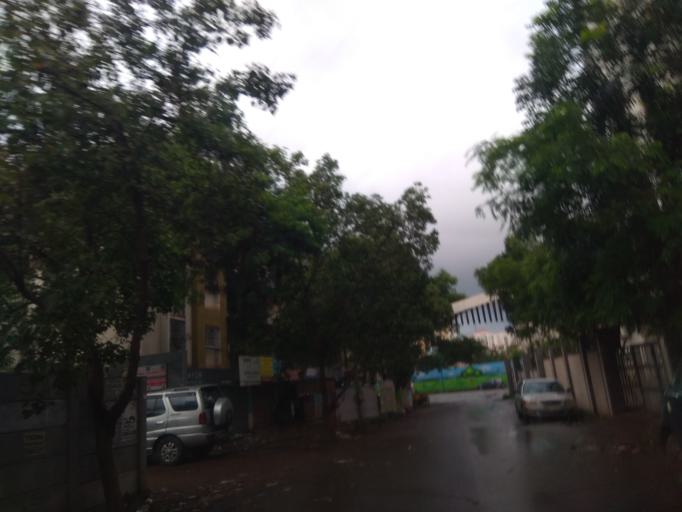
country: IN
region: Maharashtra
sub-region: Pune Division
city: Kharakvasla
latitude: 18.4892
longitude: 73.7944
